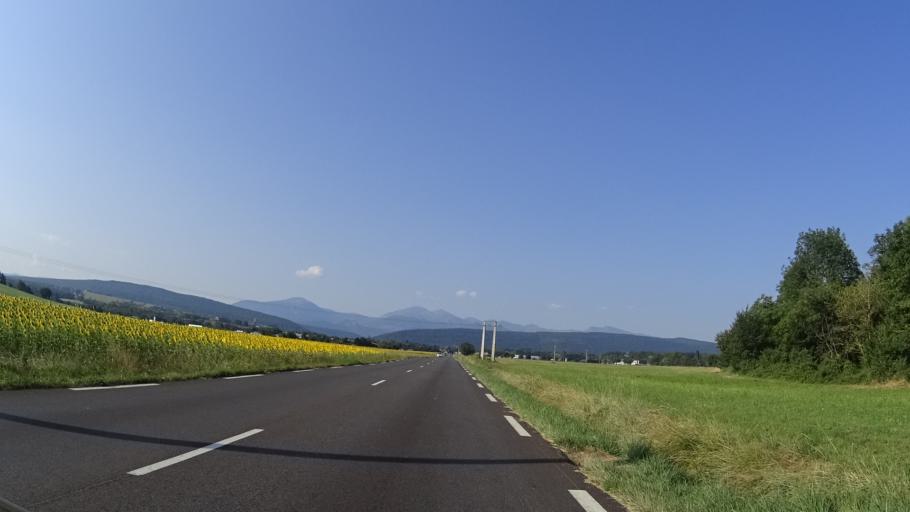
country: FR
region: Midi-Pyrenees
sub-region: Departement de l'Ariege
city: Lavelanet
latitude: 42.9918
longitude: 1.8766
